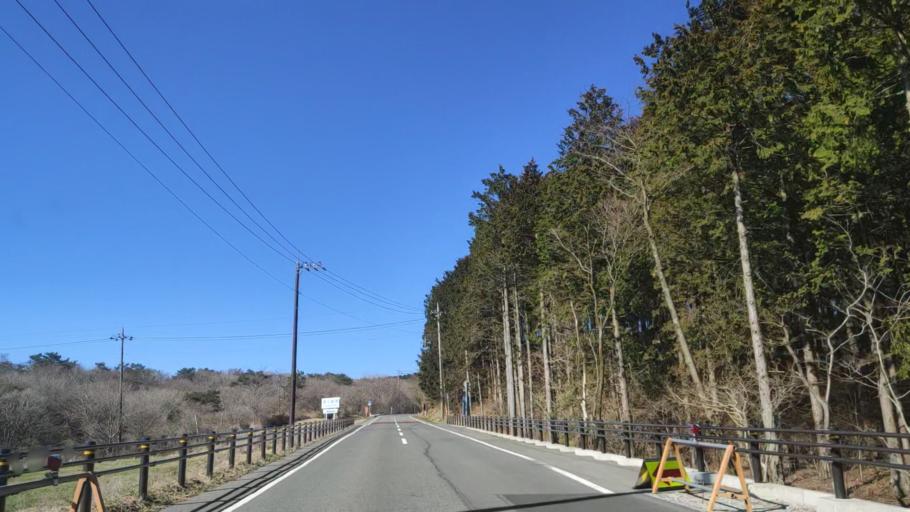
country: JP
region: Yamanashi
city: Fujikawaguchiko
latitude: 35.3836
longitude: 138.6055
